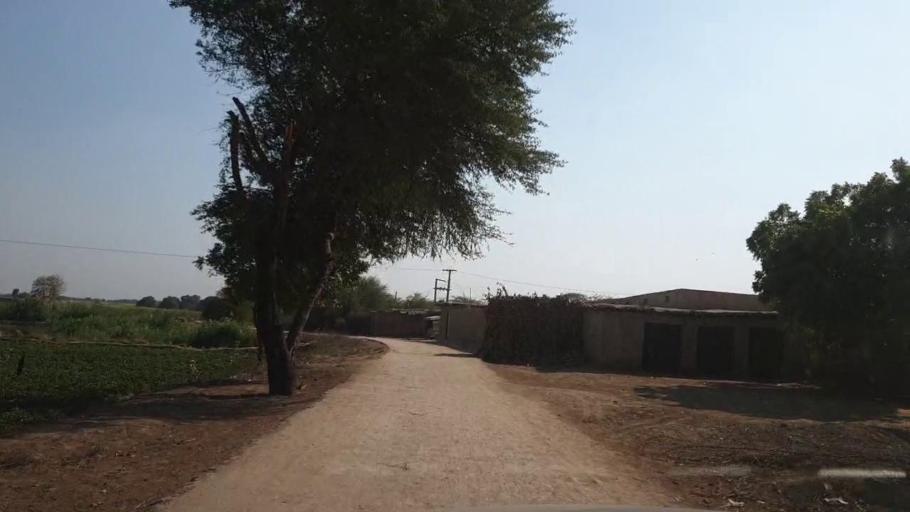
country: PK
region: Sindh
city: Tando Allahyar
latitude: 25.5856
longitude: 68.7521
